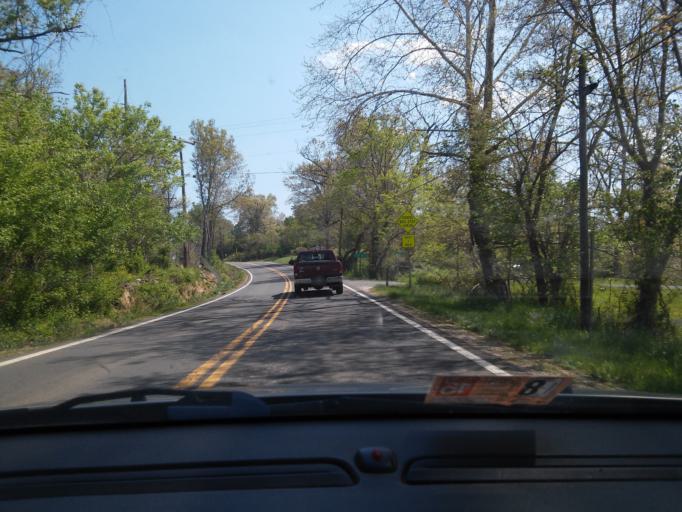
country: US
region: Virginia
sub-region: Rappahannock County
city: Washington
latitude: 38.7713
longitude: -78.1033
